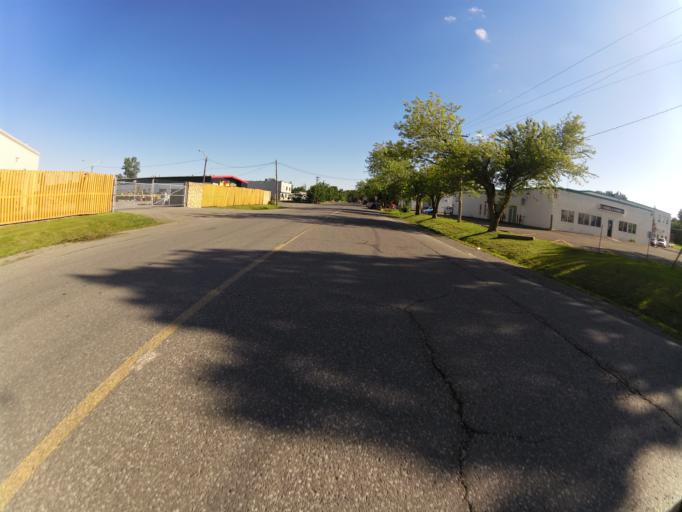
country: CA
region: Ontario
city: Ottawa
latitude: 45.3248
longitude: -75.7216
